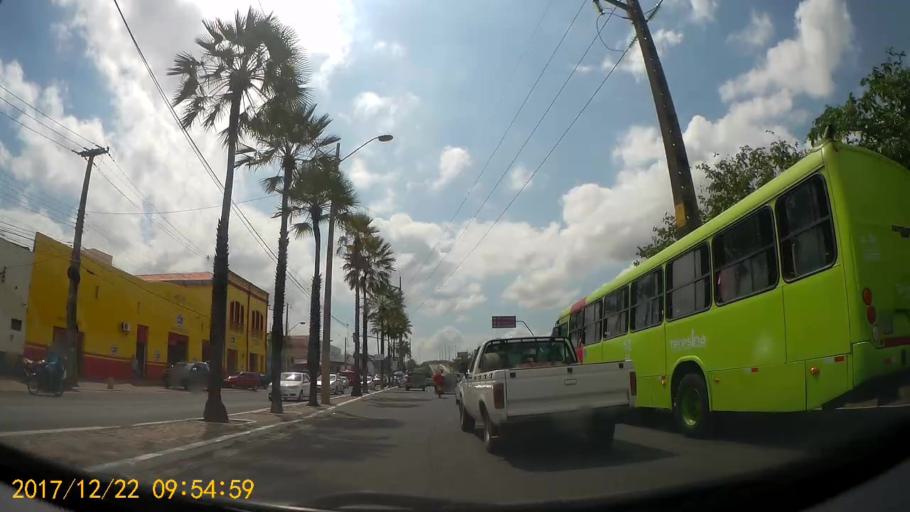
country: BR
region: Piaui
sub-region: Teresina
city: Teresina
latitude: -5.0956
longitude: -42.8171
